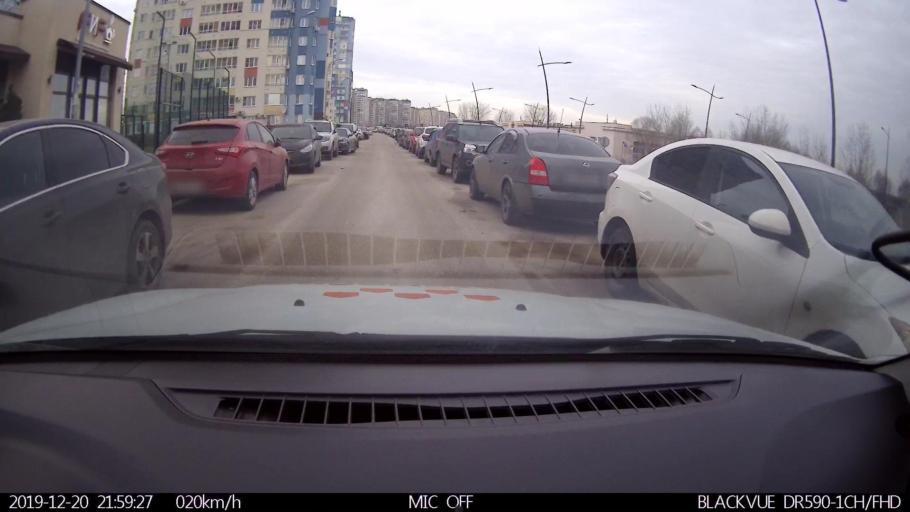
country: RU
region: Nizjnij Novgorod
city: Nizhniy Novgorod
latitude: 56.3421
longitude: 43.9541
